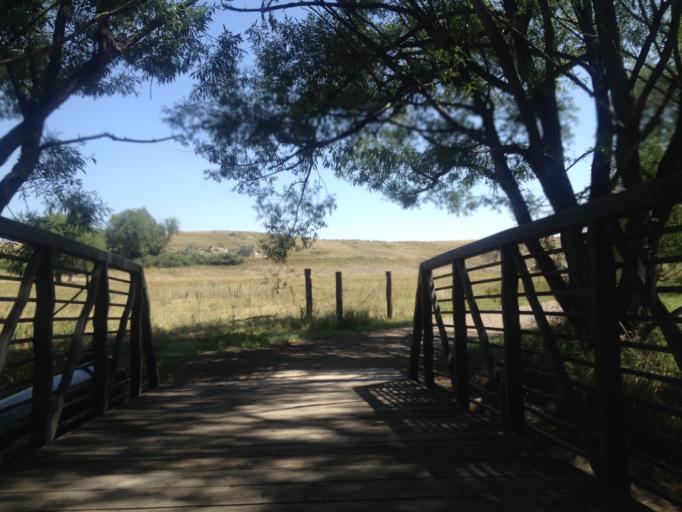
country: US
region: Colorado
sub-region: Boulder County
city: Louisville
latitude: 39.9643
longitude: -105.1405
